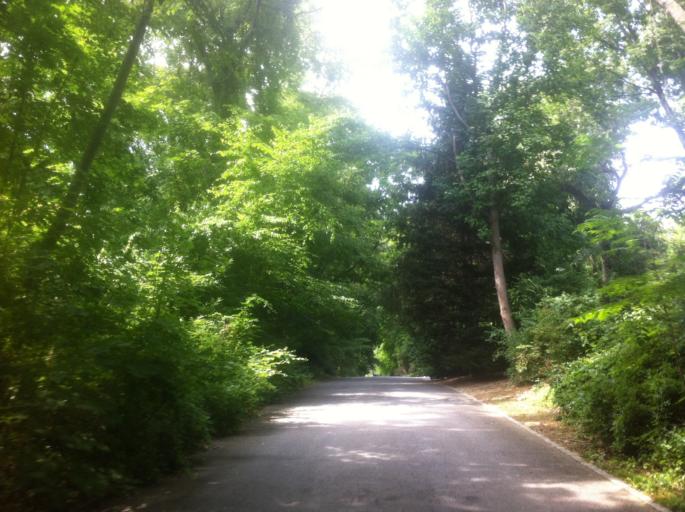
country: US
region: New York
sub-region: Nassau County
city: Upper Brookville
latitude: 40.8596
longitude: -73.5777
